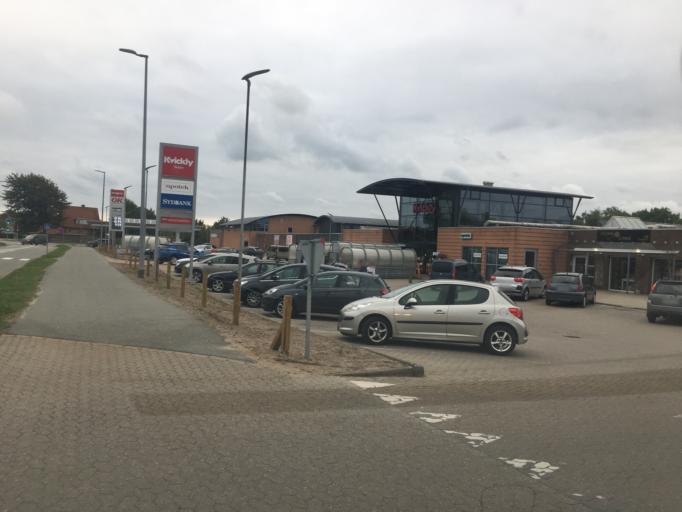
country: DK
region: South Denmark
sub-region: Tonder Kommune
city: Tonder
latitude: 54.9398
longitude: 8.8557
